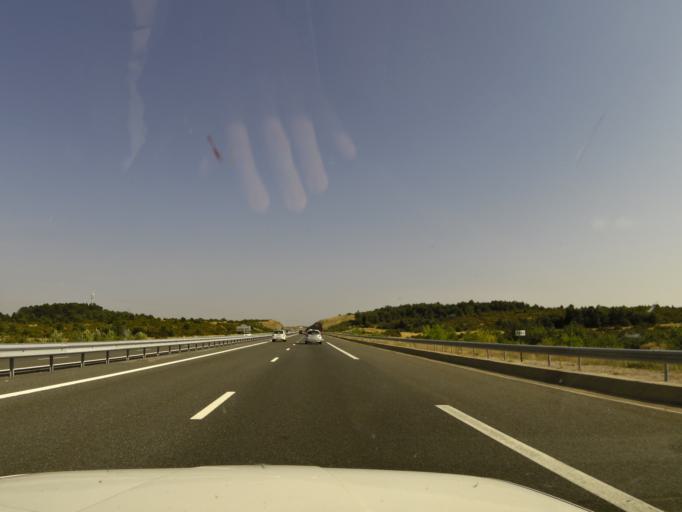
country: FR
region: Midi-Pyrenees
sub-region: Departement de l'Aveyron
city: Creissels
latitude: 44.0423
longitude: 3.0568
